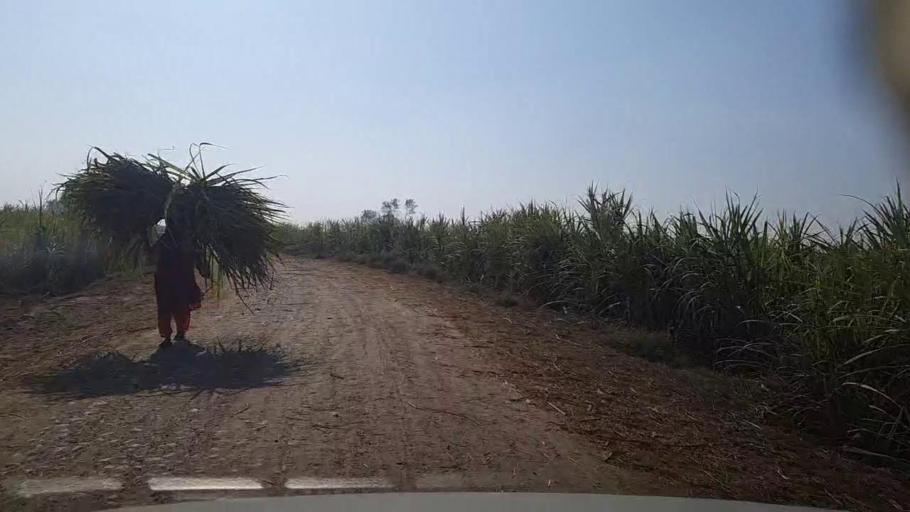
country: PK
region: Sindh
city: Mirpur Mathelo
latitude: 28.0699
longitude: 69.6173
